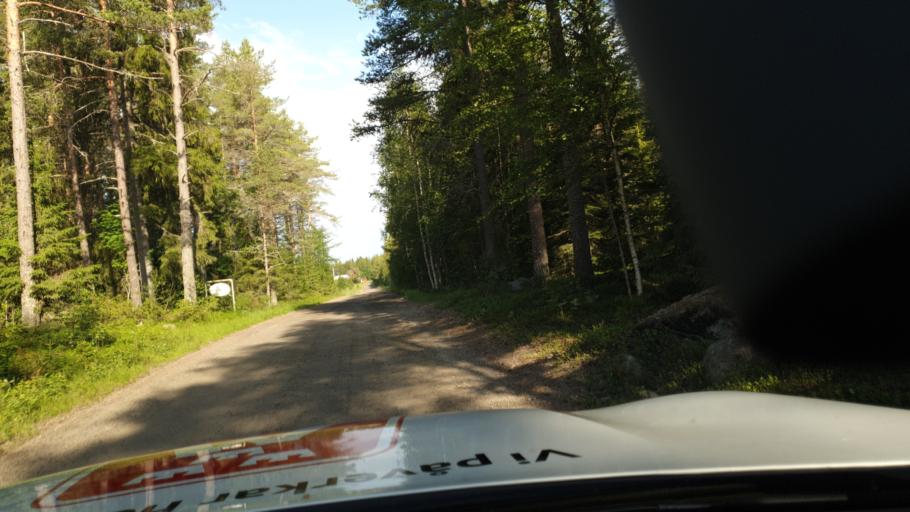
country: SE
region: Vaesterbotten
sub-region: Robertsfors Kommun
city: Robertsfors
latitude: 64.2263
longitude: 21.0638
